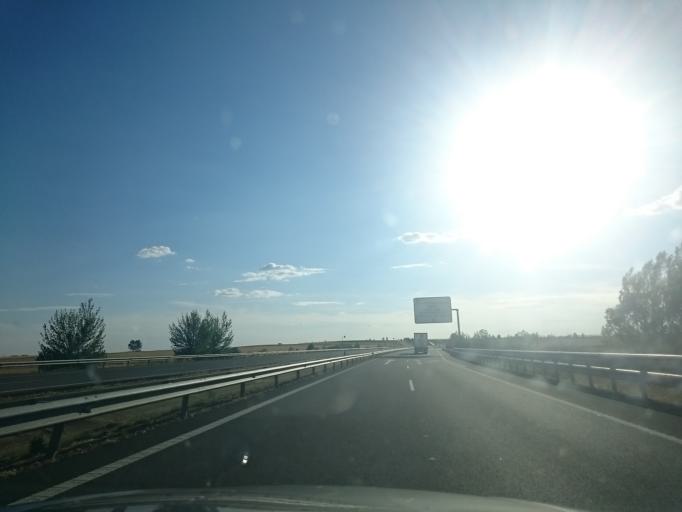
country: ES
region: Castille and Leon
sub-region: Provincia de Burgos
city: Padilla de Abajo
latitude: 42.4017
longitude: -4.2071
